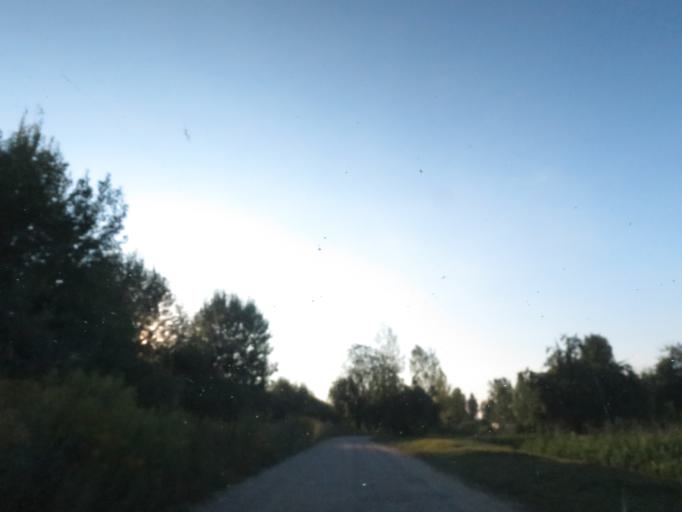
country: LV
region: Sigulda
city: Sigulda
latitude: 57.1645
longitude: 24.8247
